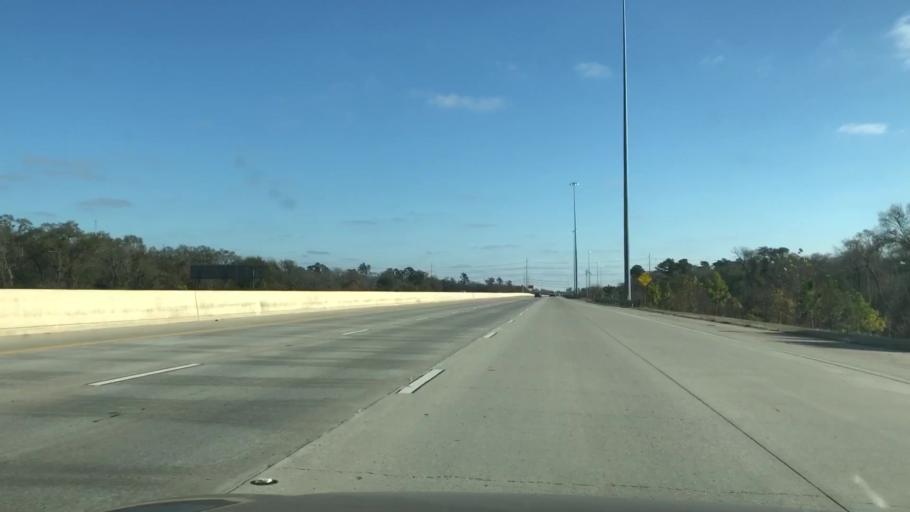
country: US
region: Texas
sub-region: Harris County
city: Jacinto City
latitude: 29.7873
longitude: -95.2420
